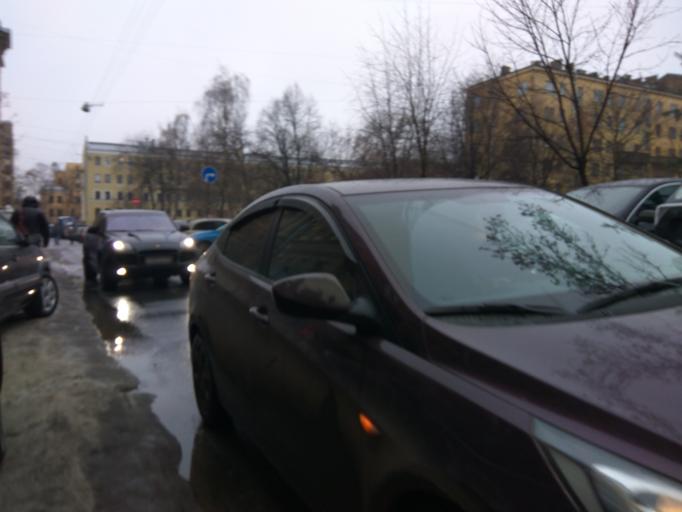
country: RU
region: St.-Petersburg
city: Centralniy
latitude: 59.9445
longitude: 30.3818
